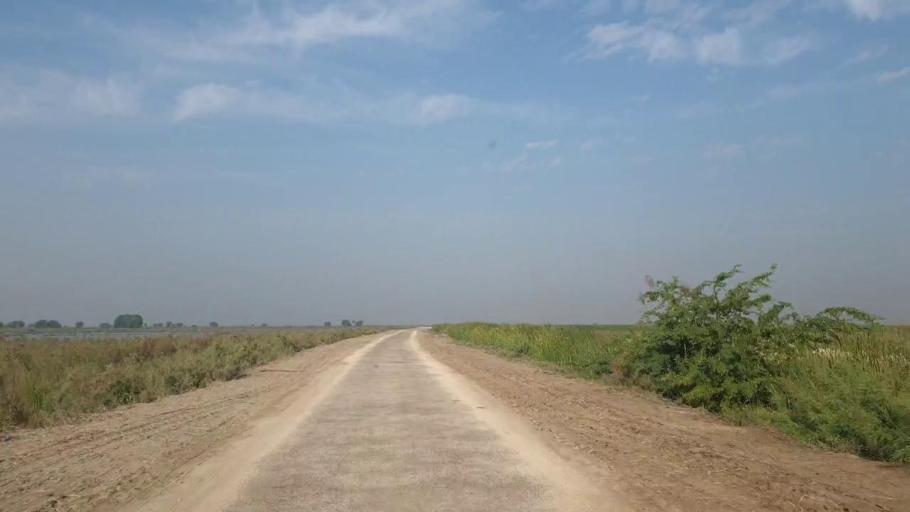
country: PK
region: Sindh
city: Tando Bago
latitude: 24.8436
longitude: 68.9795
